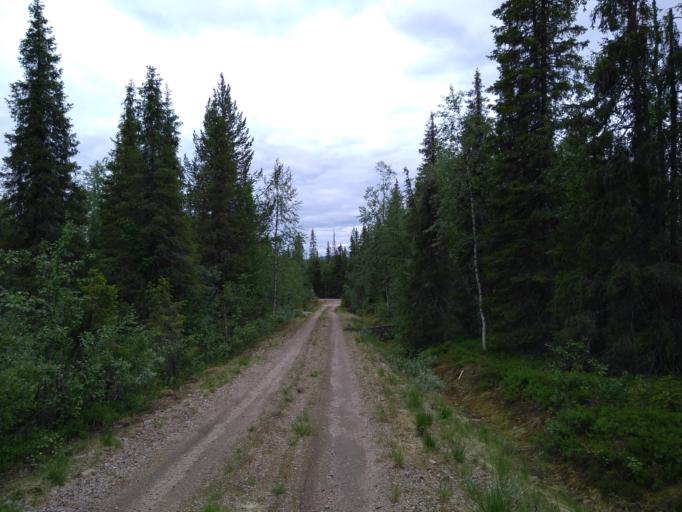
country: FI
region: Lapland
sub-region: Tunturi-Lappi
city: Muonio
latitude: 67.9635
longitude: 24.0753
